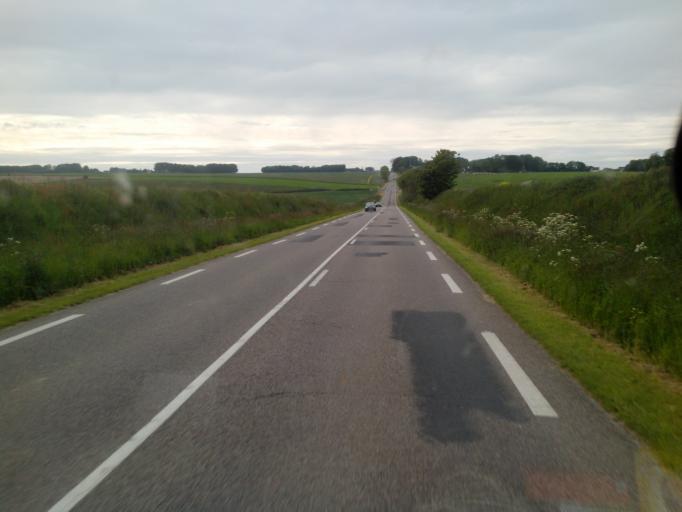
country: FR
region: Haute-Normandie
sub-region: Departement de la Seine-Maritime
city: Fauville-en-Caux
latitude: 49.6770
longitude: 0.5647
